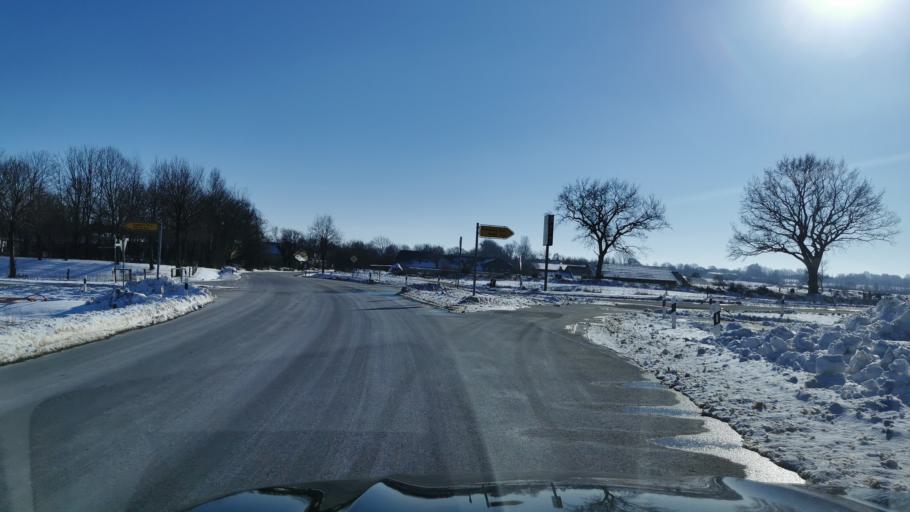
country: DE
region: Schleswig-Holstein
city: Grundhof
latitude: 54.7508
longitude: 9.6407
